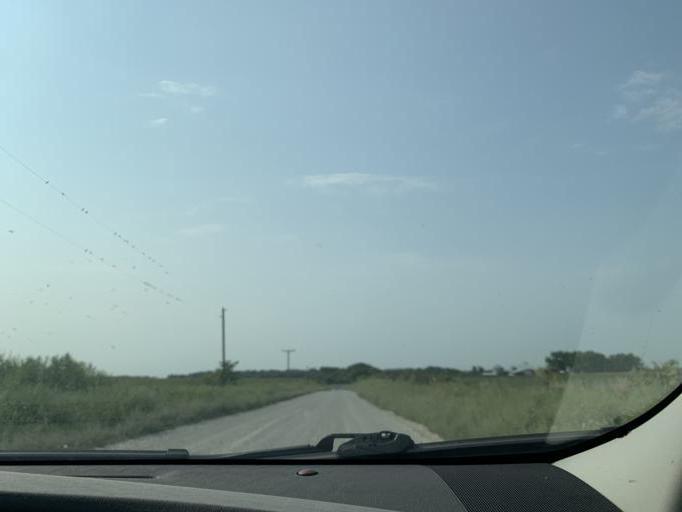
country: US
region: Illinois
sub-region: Whiteside County
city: Sterling
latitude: 41.8277
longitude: -89.7472
